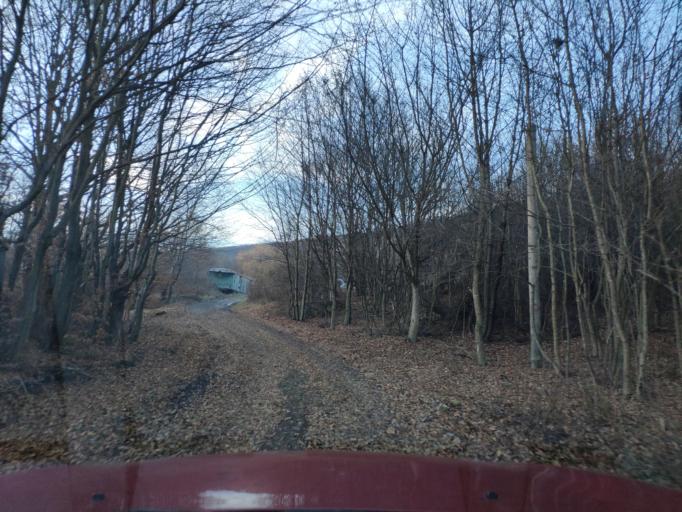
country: SK
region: Kosicky
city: Secovce
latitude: 48.6357
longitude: 21.4657
